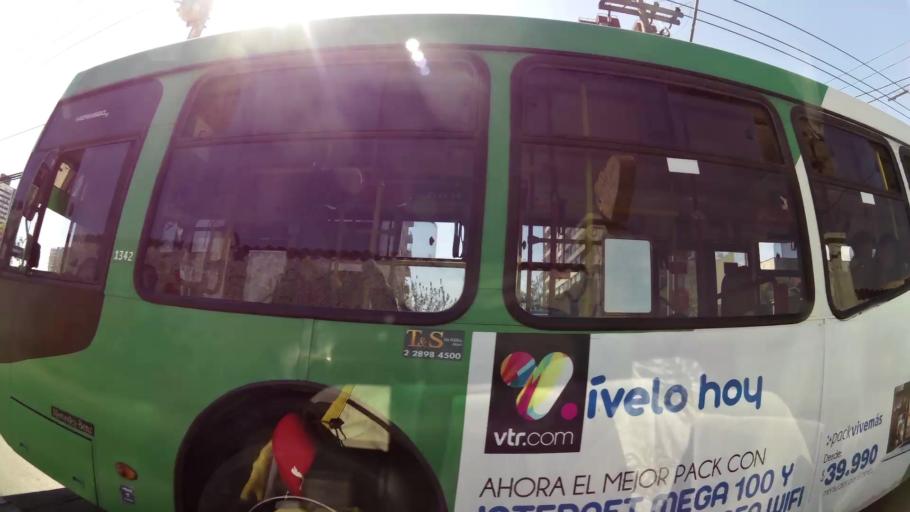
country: CL
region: Santiago Metropolitan
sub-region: Provincia de Santiago
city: Santiago
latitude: -33.5149
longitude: -70.6572
